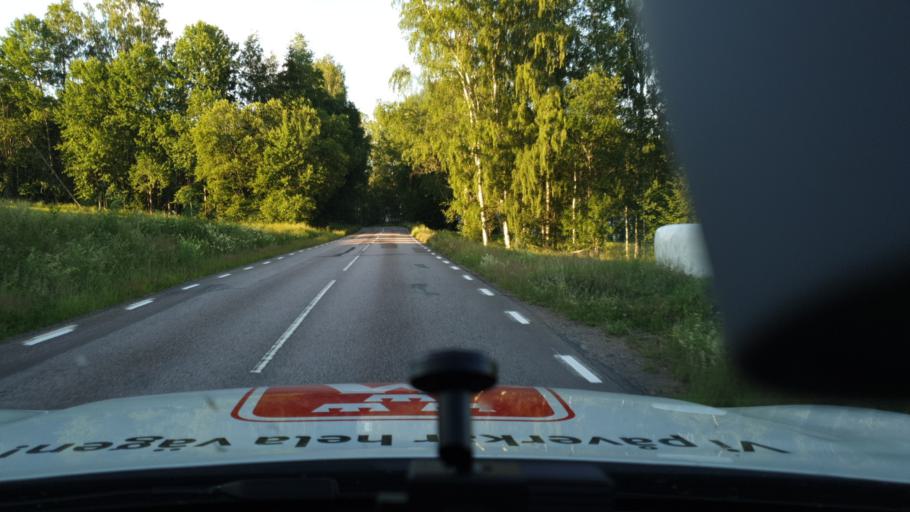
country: SE
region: Vaermland
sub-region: Kils Kommun
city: Kil
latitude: 59.5839
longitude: 13.3111
